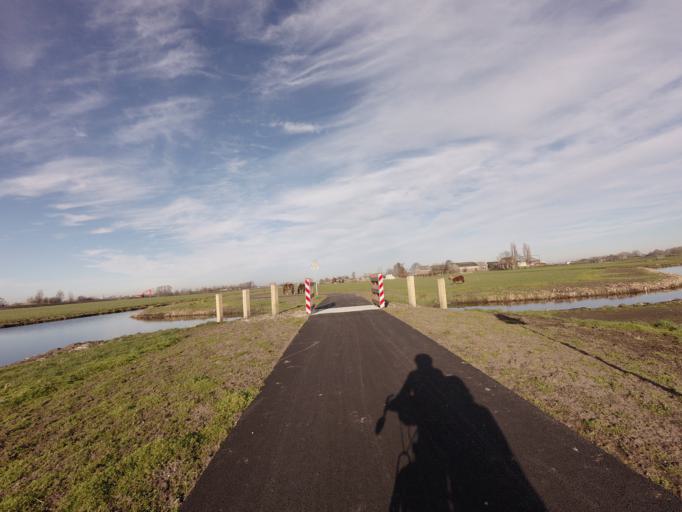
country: NL
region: South Holland
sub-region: Gemeente Leiderdorp
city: Leiderdorp
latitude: 52.1902
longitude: 4.5319
